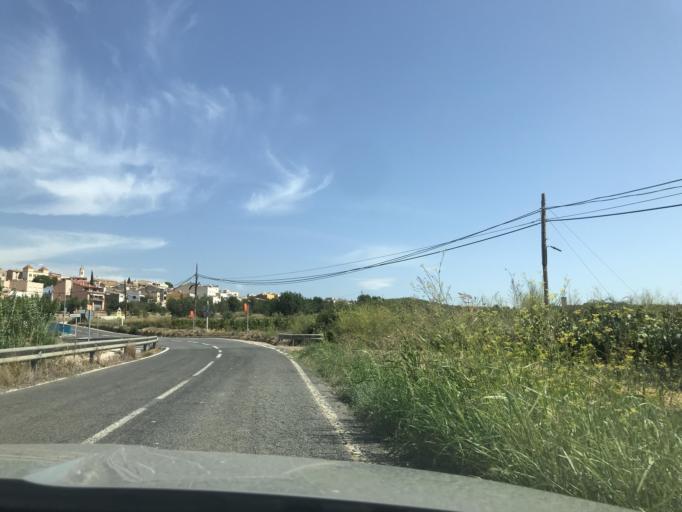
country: ES
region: Catalonia
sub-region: Provincia de Tarragona
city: Altafulla
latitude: 41.1788
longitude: 1.3728
